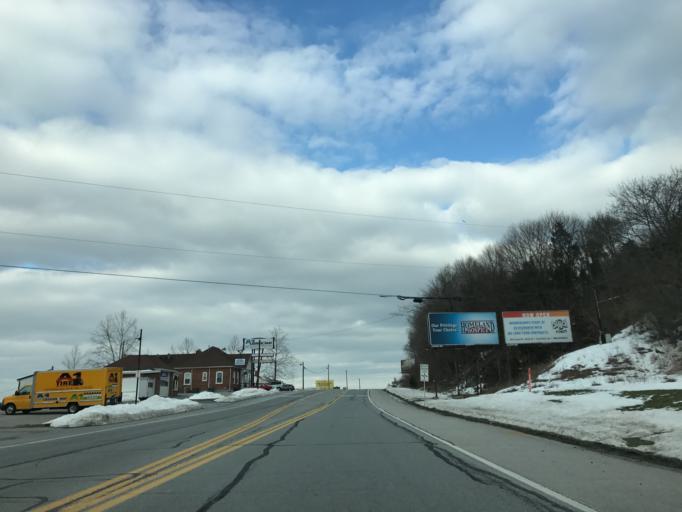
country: US
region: Pennsylvania
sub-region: York County
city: Shiloh
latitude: 39.9417
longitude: -76.7906
